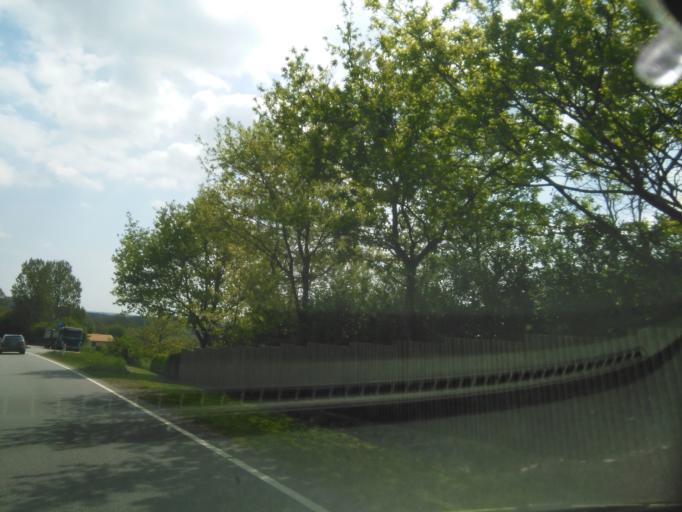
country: DK
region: Central Jutland
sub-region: Skanderborg Kommune
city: Stilling
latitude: 56.0179
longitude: 9.9801
